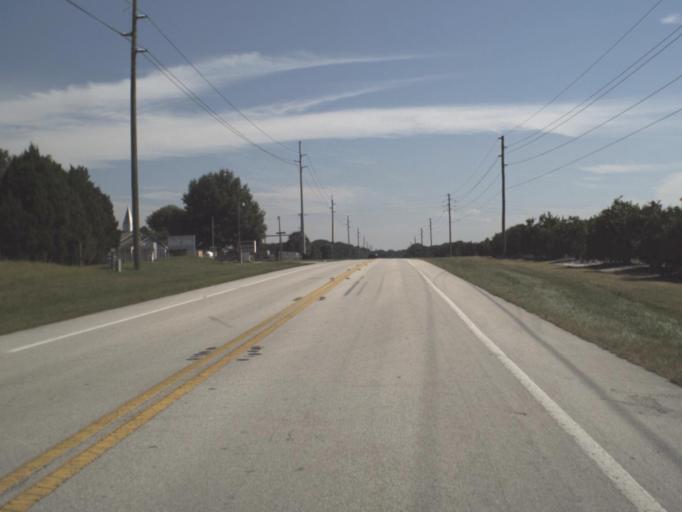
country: US
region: Florida
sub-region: Highlands County
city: Avon Park
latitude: 27.5628
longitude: -81.6472
